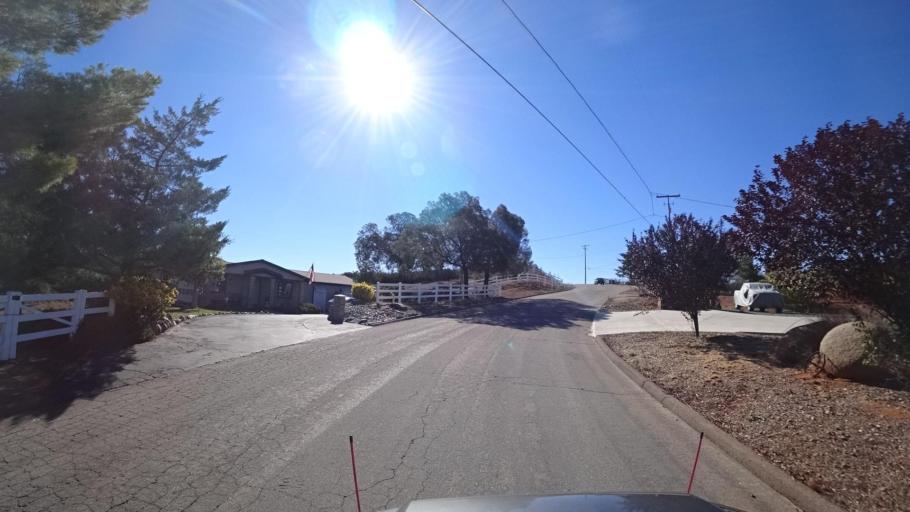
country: US
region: California
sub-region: San Diego County
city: Alpine
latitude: 32.8360
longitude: -116.7006
